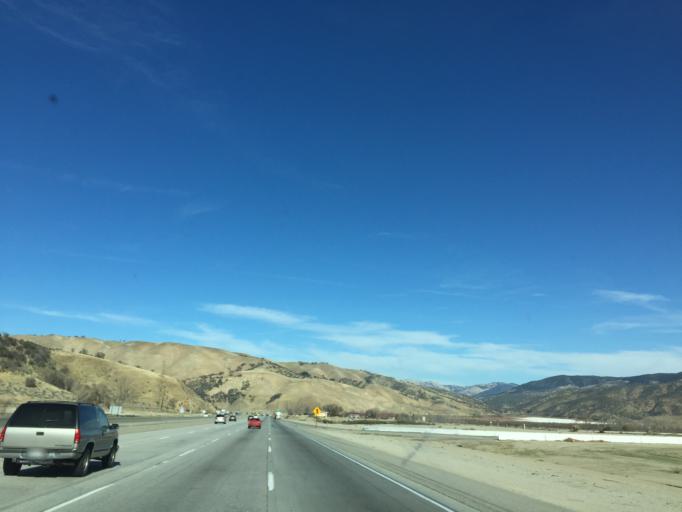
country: US
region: California
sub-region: Kern County
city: Lebec
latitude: 34.8263
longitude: -118.8726
